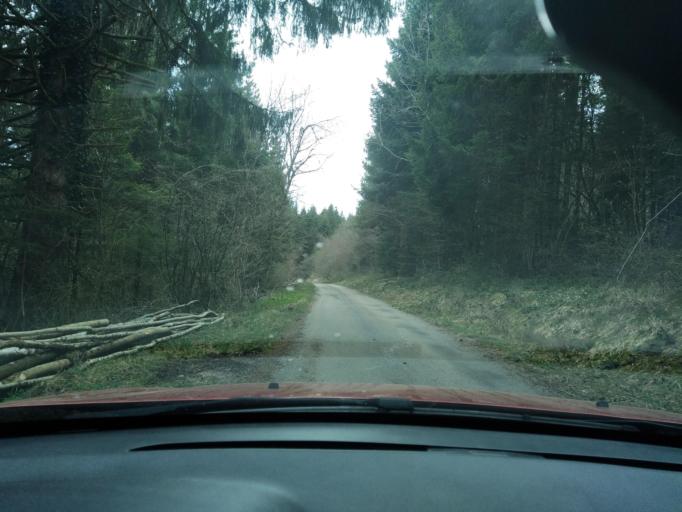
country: FR
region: Franche-Comte
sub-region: Departement du Jura
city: Moirans-en-Montagne
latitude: 46.4635
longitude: 5.7615
